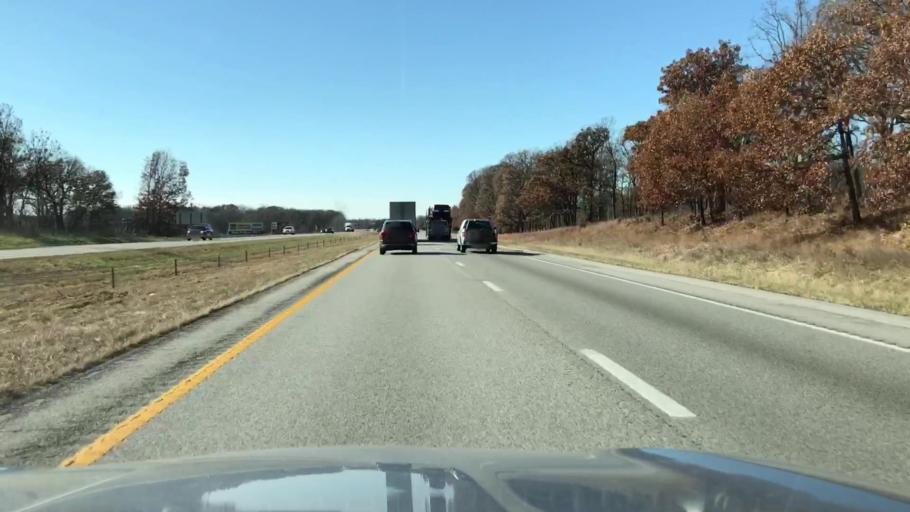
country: US
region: Missouri
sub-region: Jasper County
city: Duenweg
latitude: 37.0823
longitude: -94.3541
